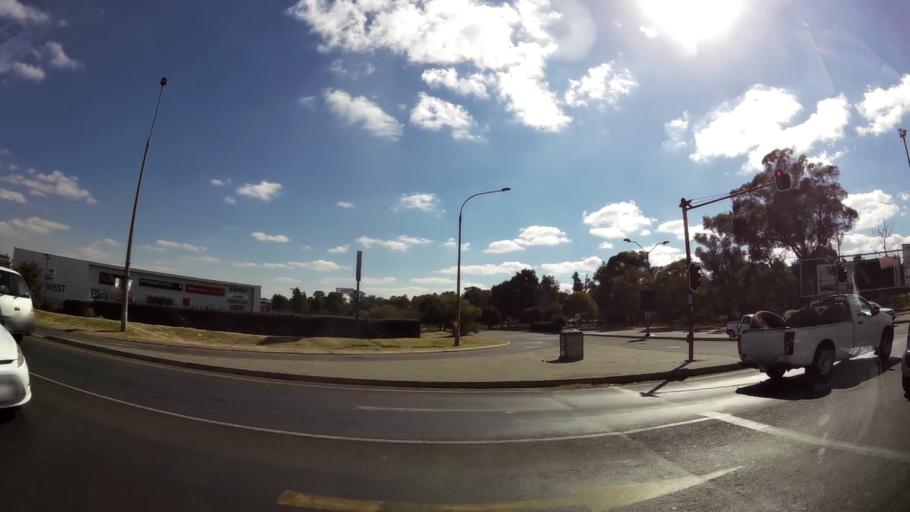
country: ZA
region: Gauteng
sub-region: West Rand District Municipality
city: Krugersdorp
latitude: -26.0878
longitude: 27.7847
